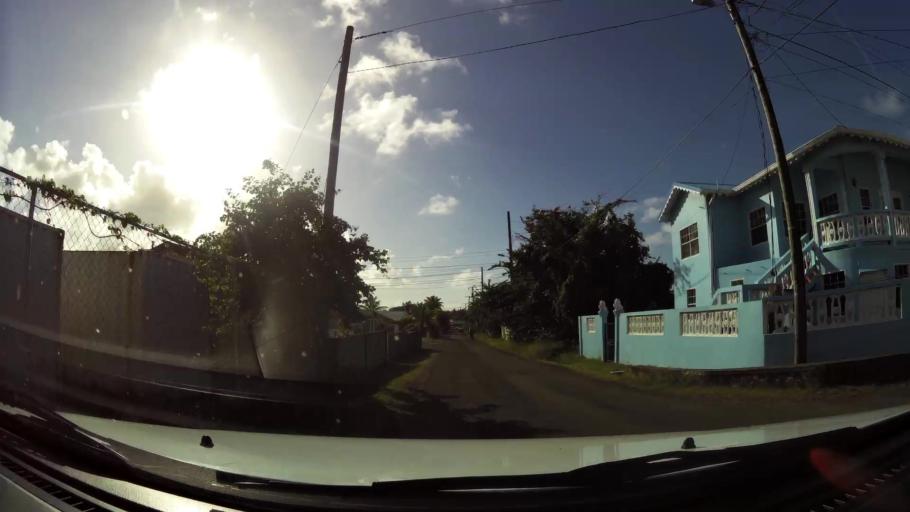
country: LC
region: Gros-Islet
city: Gros Islet
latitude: 14.0799
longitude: -60.9495
